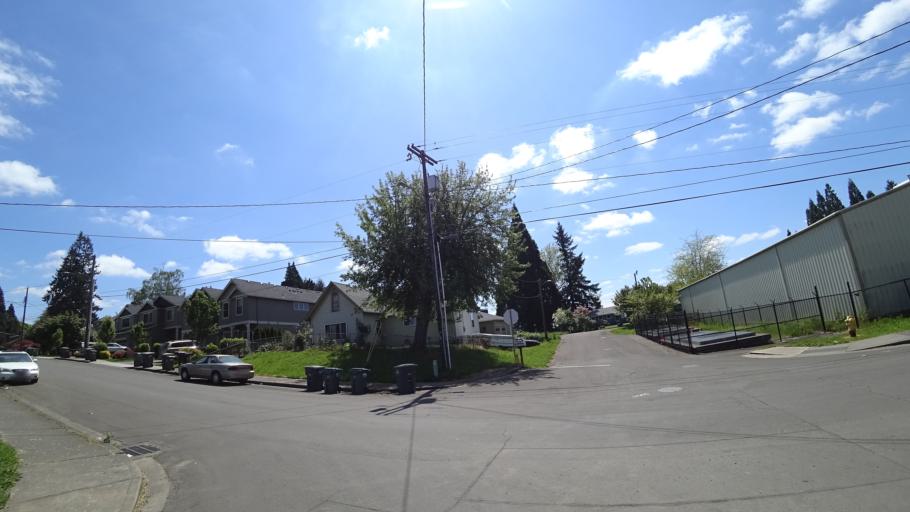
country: US
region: Oregon
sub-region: Washington County
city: Hillsboro
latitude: 45.5151
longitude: -122.9881
